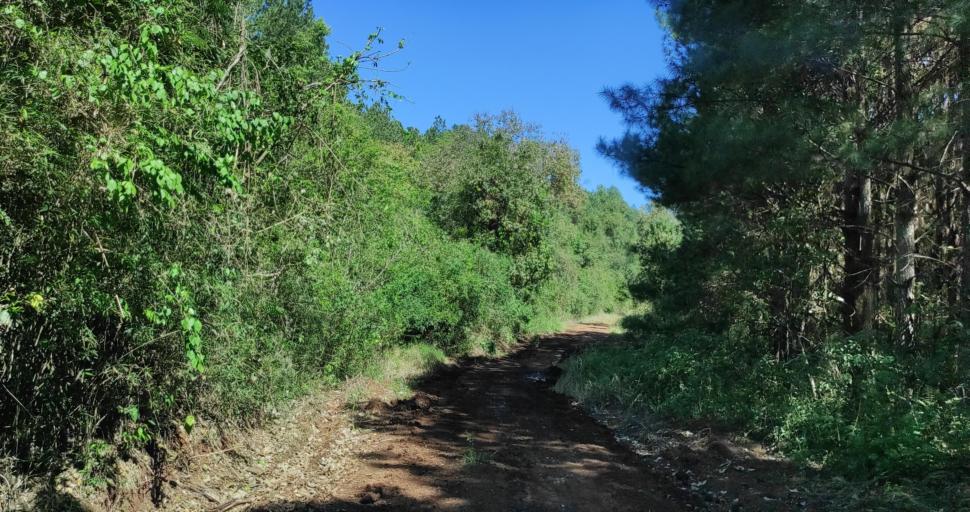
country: AR
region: Misiones
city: Ruiz de Montoya
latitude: -26.9497
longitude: -54.9808
